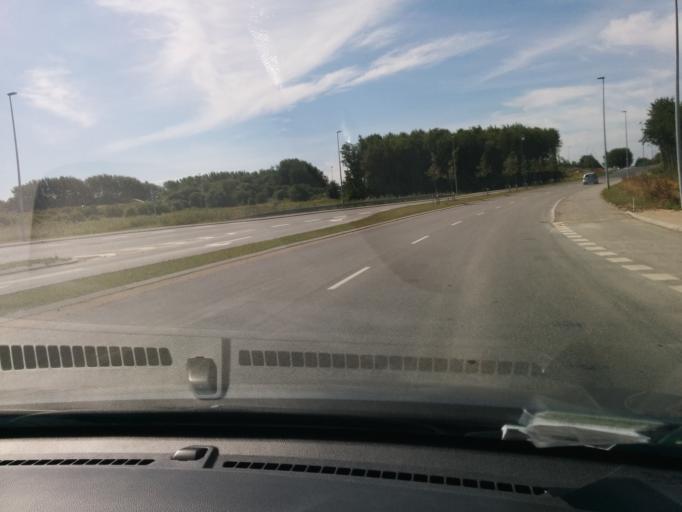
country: DK
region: Central Jutland
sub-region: Arhus Kommune
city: Arhus
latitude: 56.1859
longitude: 10.1705
